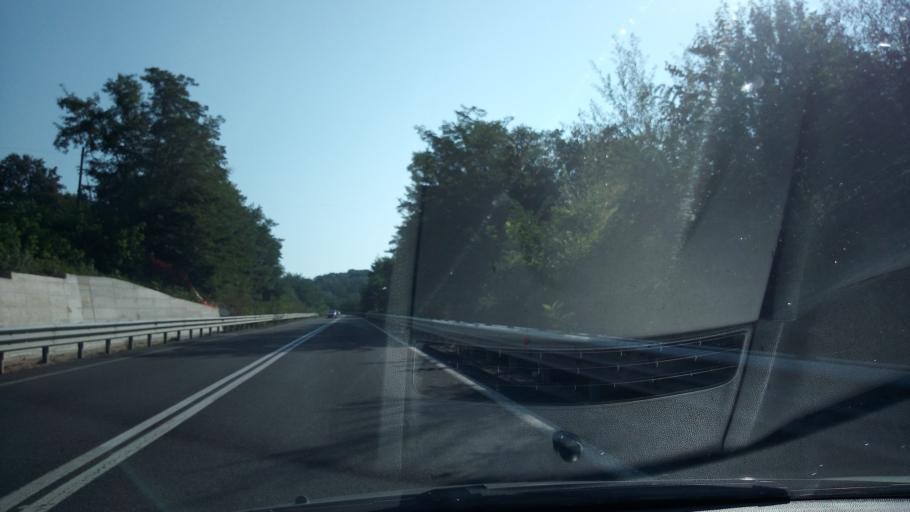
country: IT
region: Campania
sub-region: Provincia di Avellino
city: San Potito Ultra
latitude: 40.9303
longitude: 14.8687
